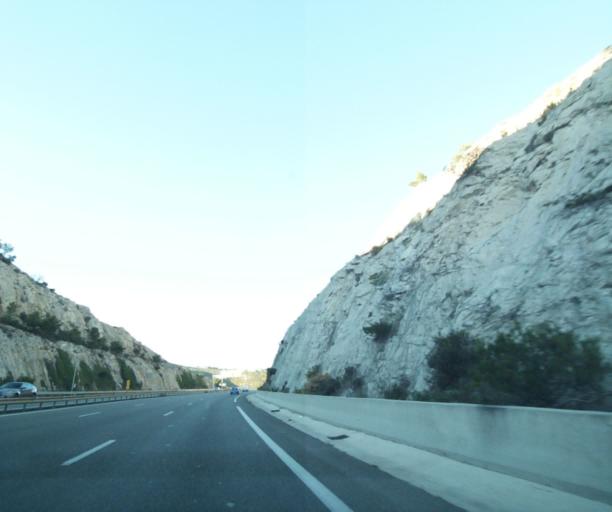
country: FR
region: Provence-Alpes-Cote d'Azur
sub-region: Departement des Bouches-du-Rhone
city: Cassis
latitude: 43.2108
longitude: 5.5831
